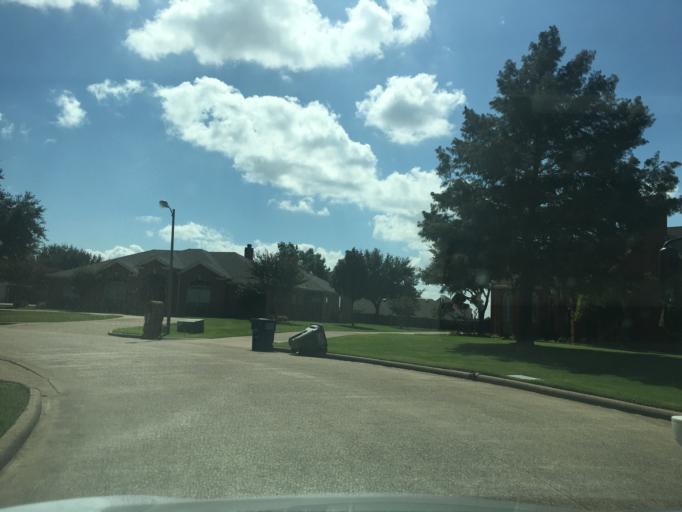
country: US
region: Texas
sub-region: Dallas County
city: Sachse
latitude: 32.9702
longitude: -96.5733
